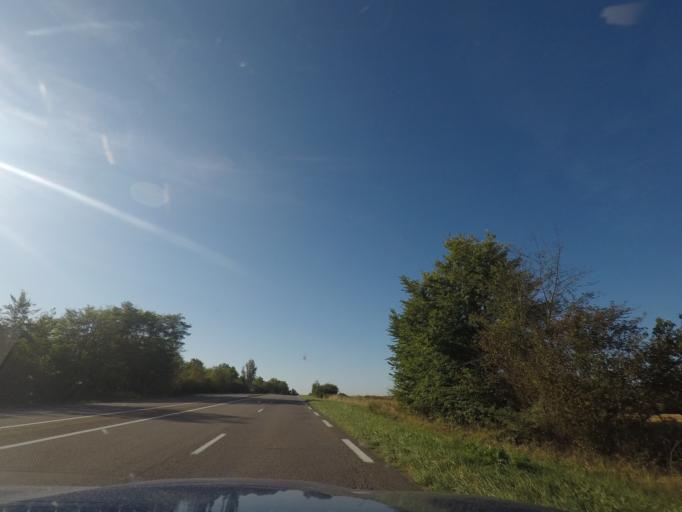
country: FR
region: Lorraine
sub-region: Departement de la Moselle
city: Hettange-Grande
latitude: 49.4318
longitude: 6.1664
